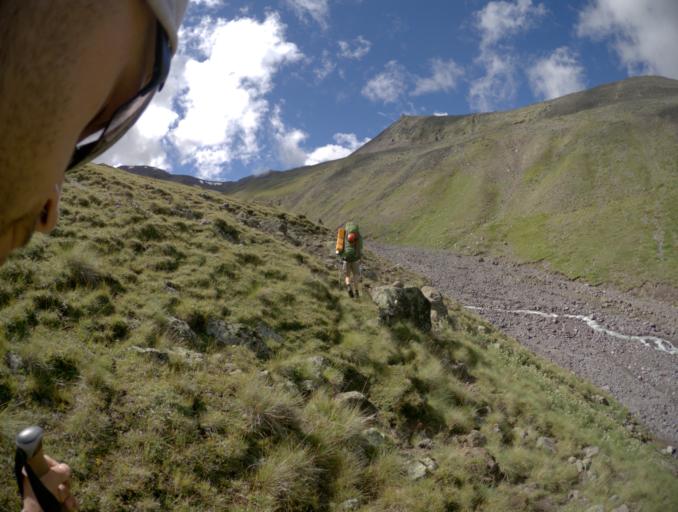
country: RU
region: Kabardino-Balkariya
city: Terskol
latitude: 43.3919
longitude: 42.3618
